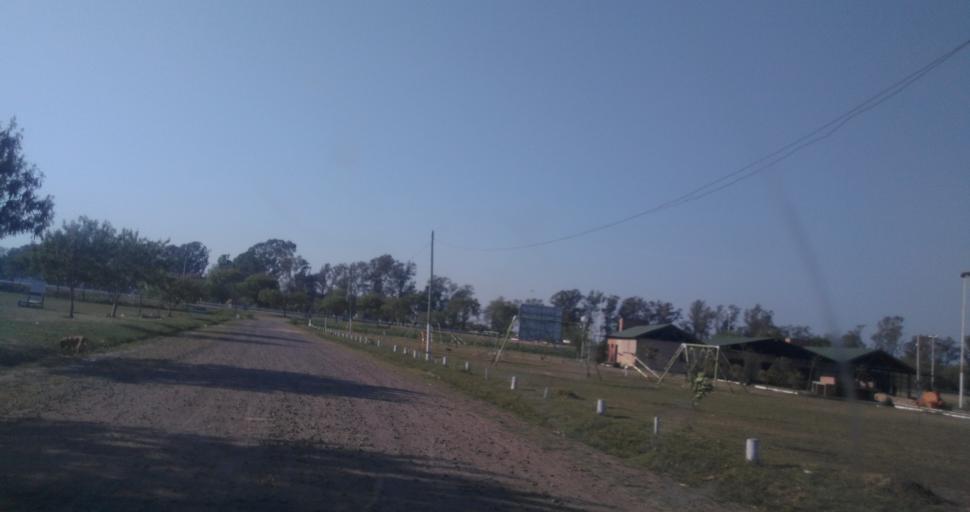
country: AR
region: Chaco
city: Fontana
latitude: -27.4392
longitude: -59.0328
